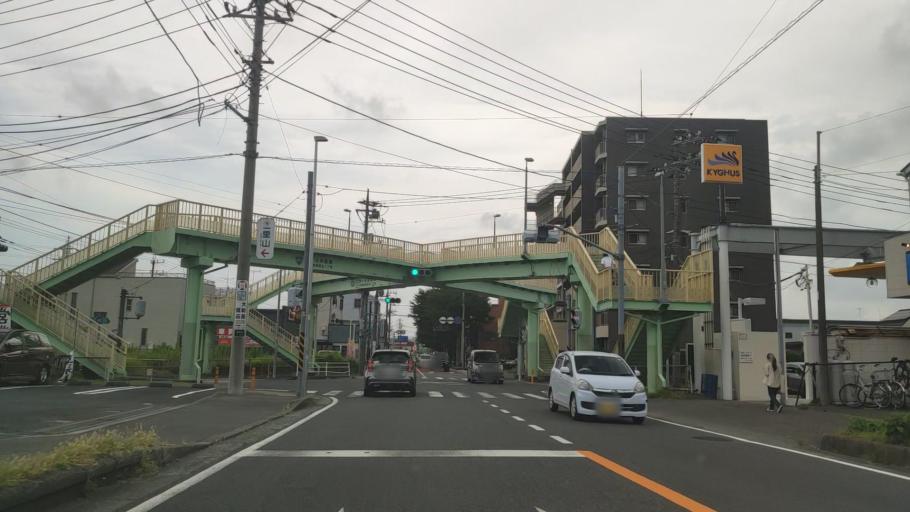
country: JP
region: Kanagawa
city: Minami-rinkan
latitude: 35.4634
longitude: 139.4671
